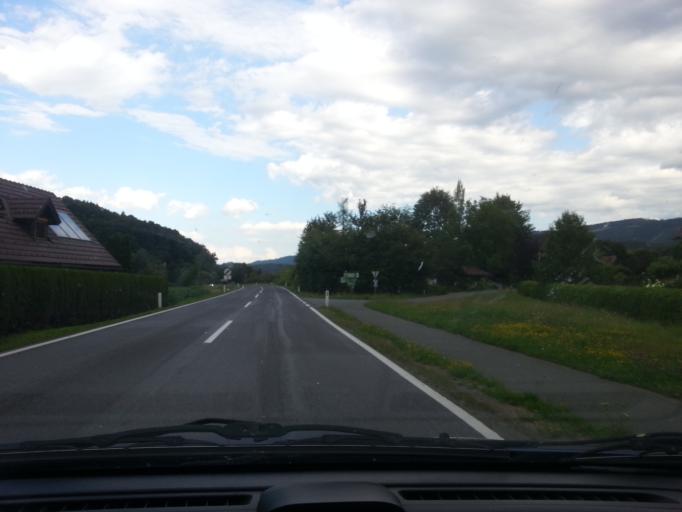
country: AT
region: Styria
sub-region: Politischer Bezirk Leibnitz
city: Oberhaag
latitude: 46.6928
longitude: 15.3207
